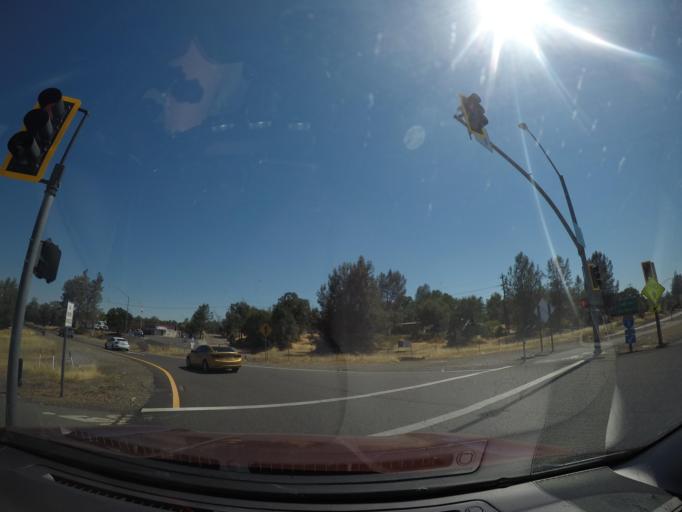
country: US
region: California
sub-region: Shasta County
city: Redding
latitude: 40.6117
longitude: -122.3659
